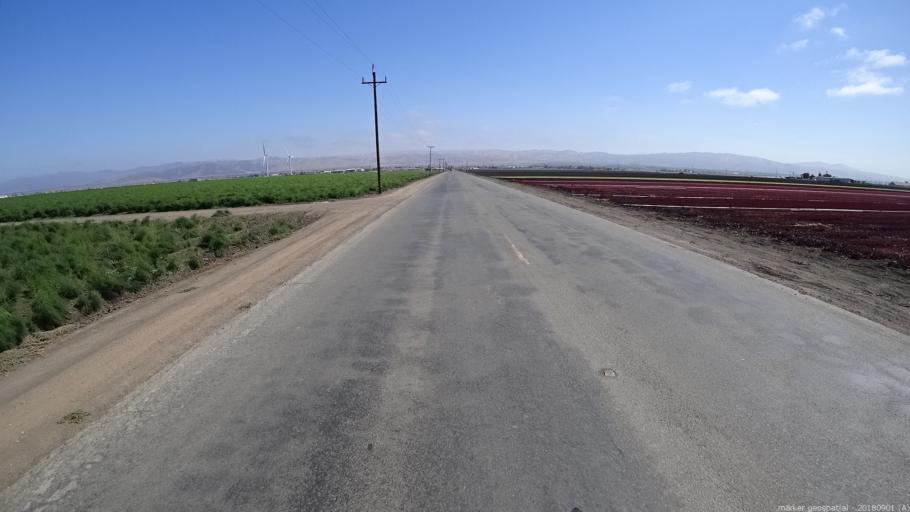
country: US
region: California
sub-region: Monterey County
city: Gonzales
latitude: 36.4917
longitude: -121.4601
